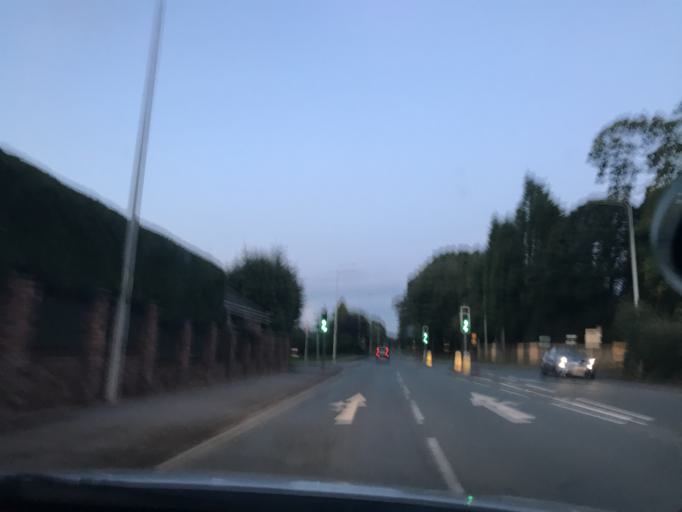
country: GB
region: England
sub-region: Cheshire West and Chester
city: Cuddington
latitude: 53.2309
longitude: -2.5955
